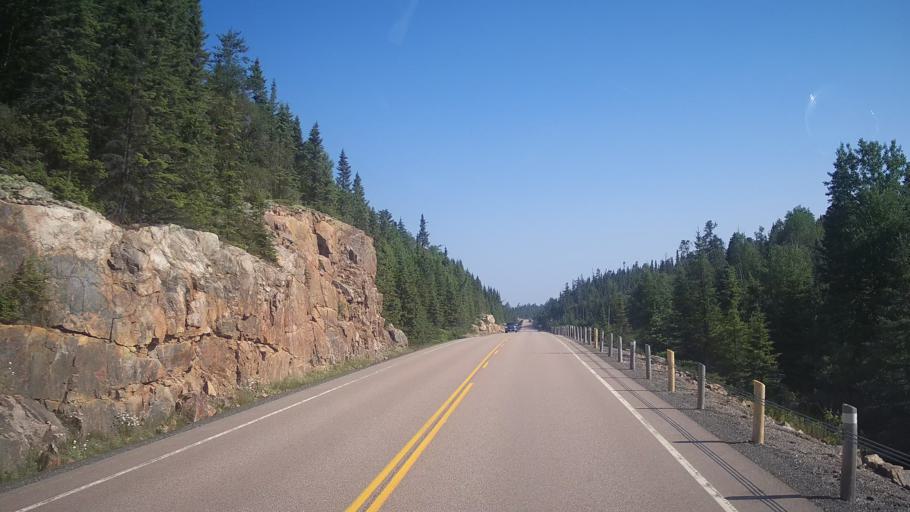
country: CA
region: Ontario
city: Rayside-Balfour
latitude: 46.9999
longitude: -81.6325
